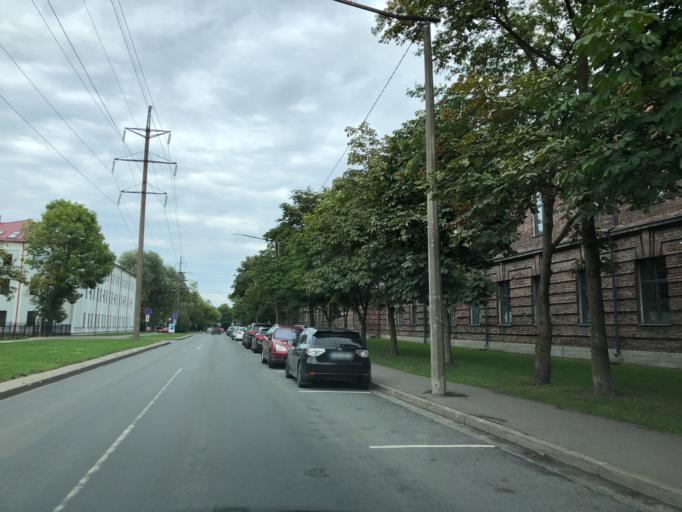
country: EE
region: Harju
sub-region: Tallinna linn
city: Tallinn
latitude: 59.4512
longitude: 24.7156
